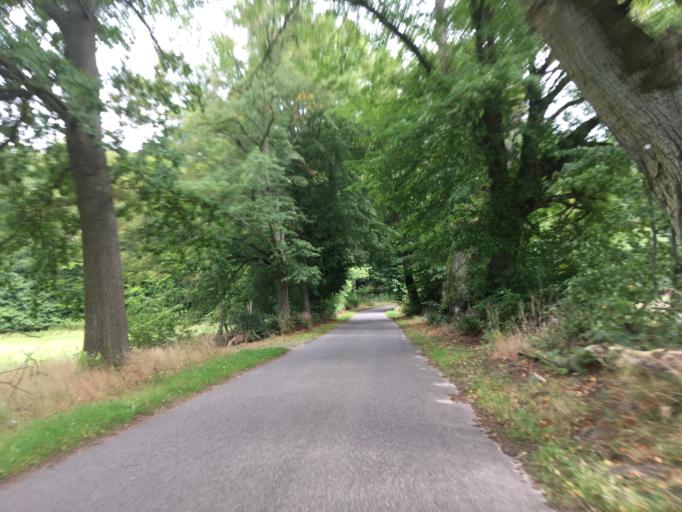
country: DE
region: Brandenburg
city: Althuttendorf
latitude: 53.0213
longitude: 13.7943
